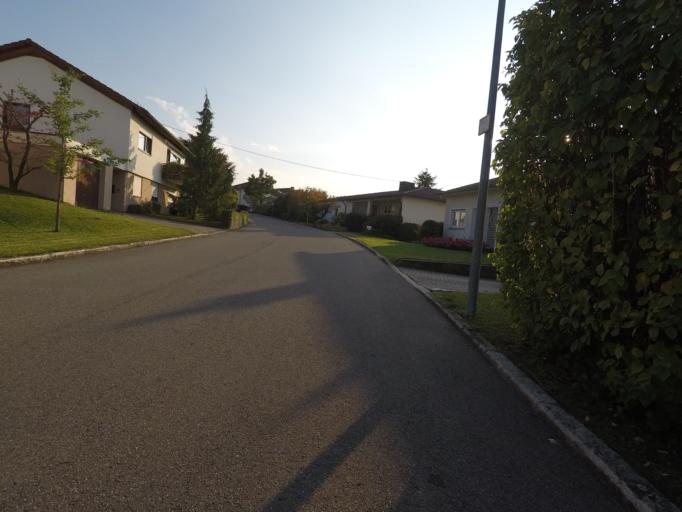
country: DE
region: Baden-Wuerttemberg
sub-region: Tuebingen Region
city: Pfullingen
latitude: 48.4686
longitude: 9.2360
